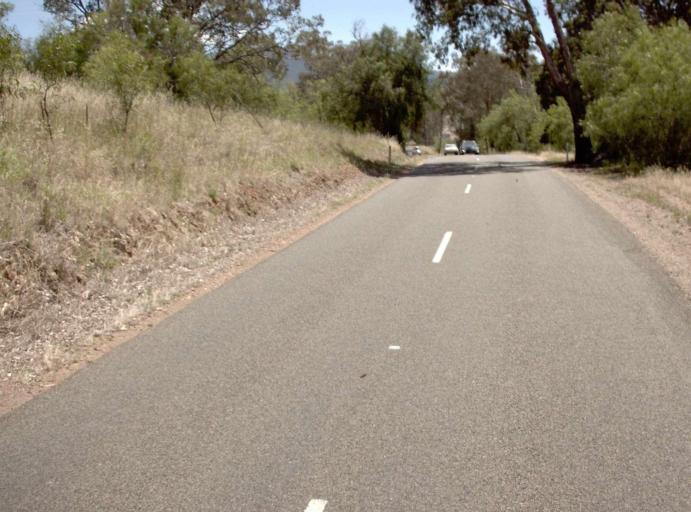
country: AU
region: Victoria
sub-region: East Gippsland
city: Bairnsdale
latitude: -37.2116
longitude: 147.7177
